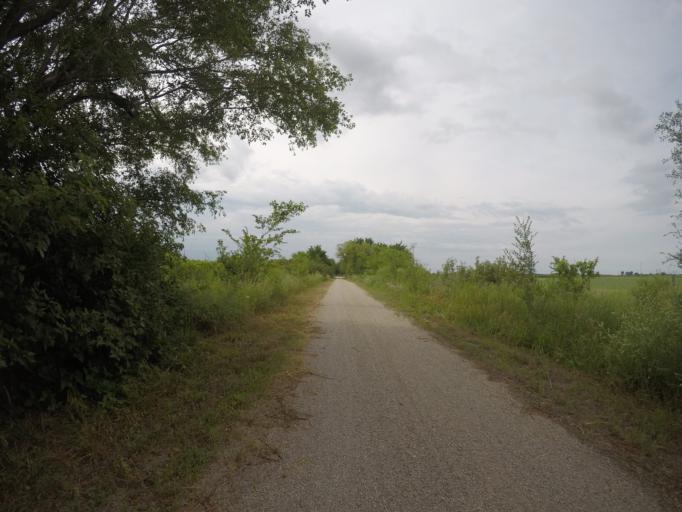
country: US
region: Kansas
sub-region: Franklin County
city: Ottawa
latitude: 38.5076
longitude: -95.2728
